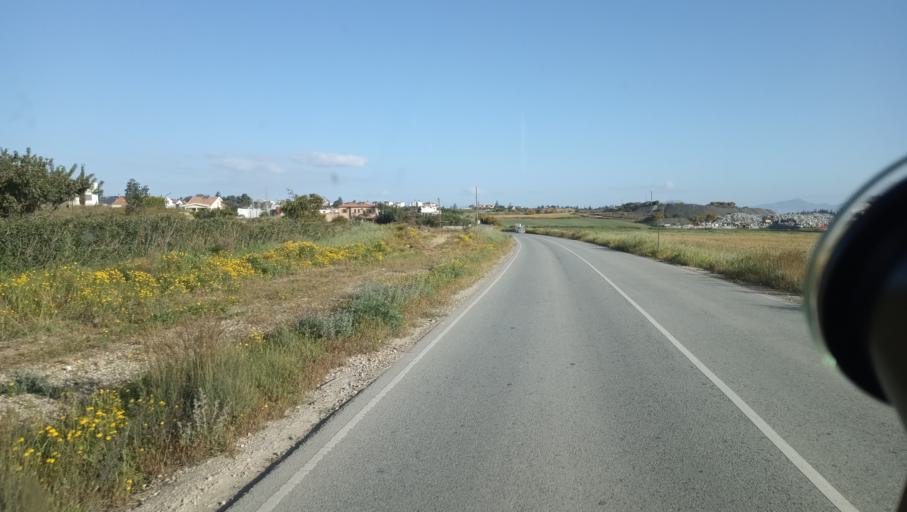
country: CY
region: Lefkosia
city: Geri
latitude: 35.0756
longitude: 33.3999
